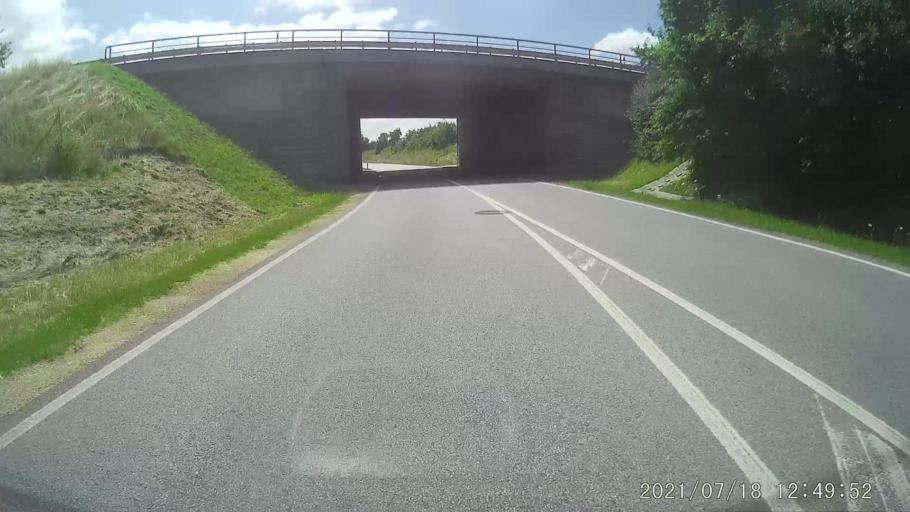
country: DE
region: Saxony
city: Reichenbach
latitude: 51.2038
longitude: 14.7608
